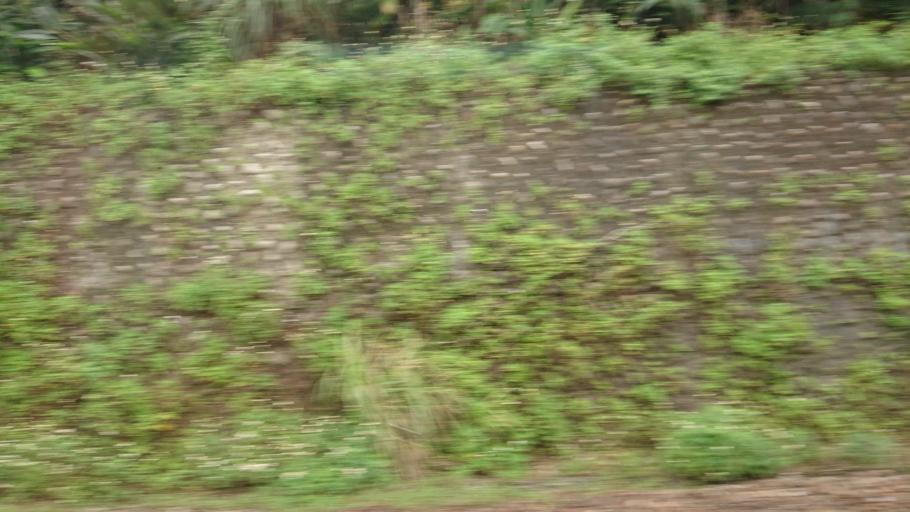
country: TW
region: Taiwan
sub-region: Yilan
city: Yilan
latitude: 24.9209
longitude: 121.8829
